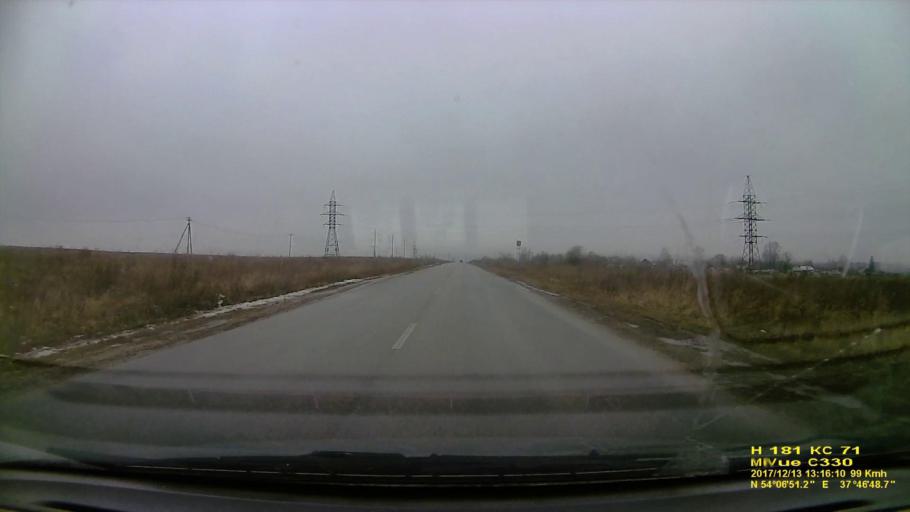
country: RU
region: Tula
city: Bolokhovo
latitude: 54.1143
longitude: 37.7798
